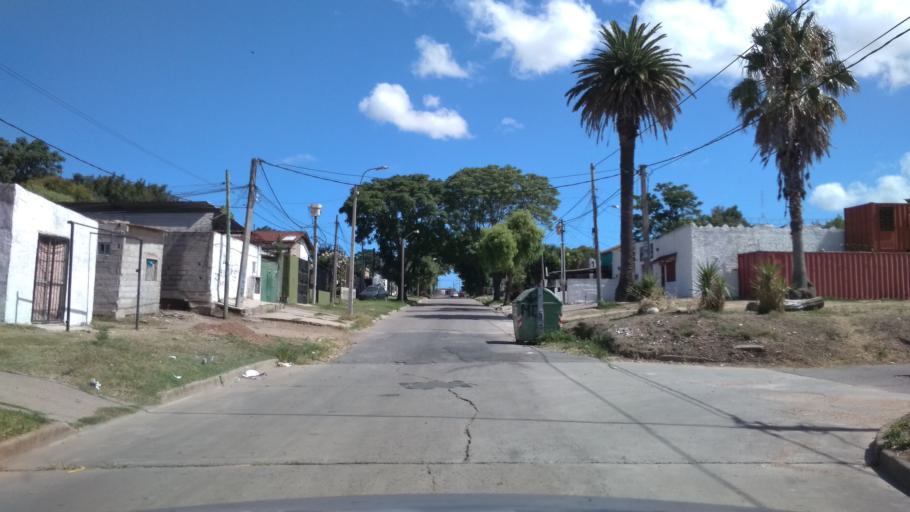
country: UY
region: Canelones
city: La Paz
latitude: -34.8271
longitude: -56.2230
